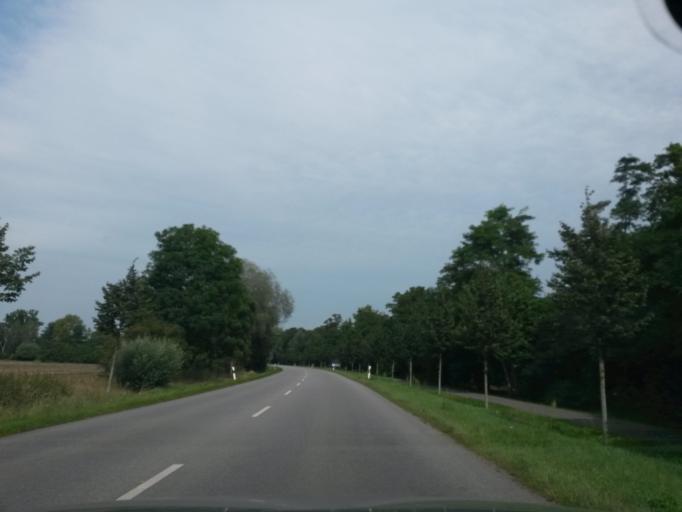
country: DE
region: Brandenburg
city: Schwedt (Oder)
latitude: 53.0496
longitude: 14.2705
